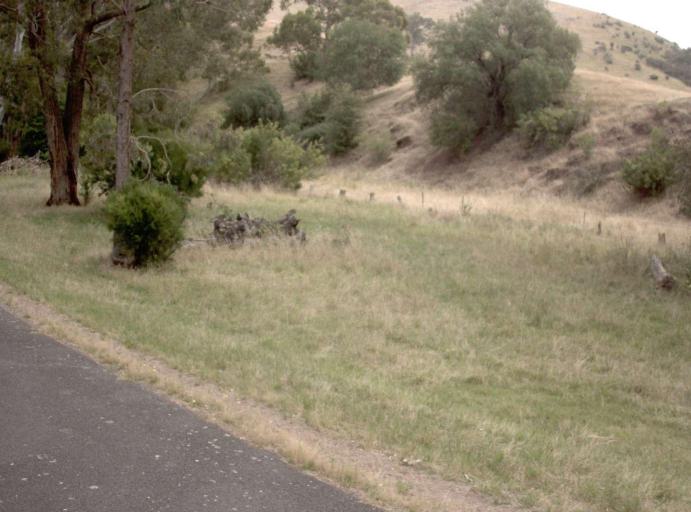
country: AU
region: Victoria
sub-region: Wellington
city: Heyfield
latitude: -37.6443
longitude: 146.6396
